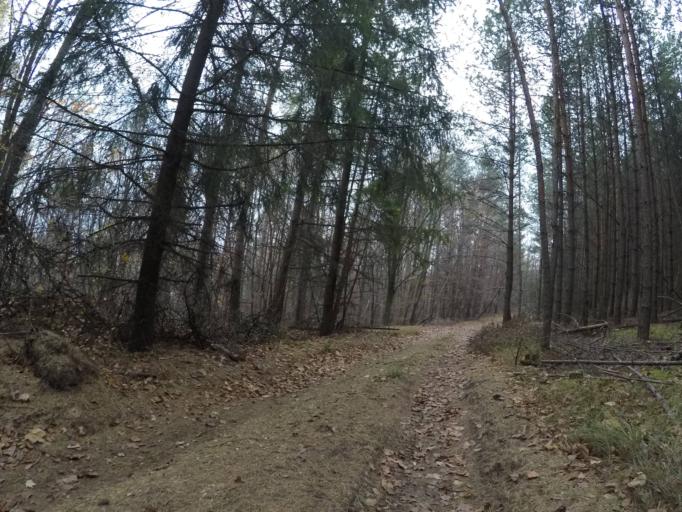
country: SK
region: Presovsky
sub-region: Okres Presov
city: Presov
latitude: 48.8978
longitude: 21.1715
